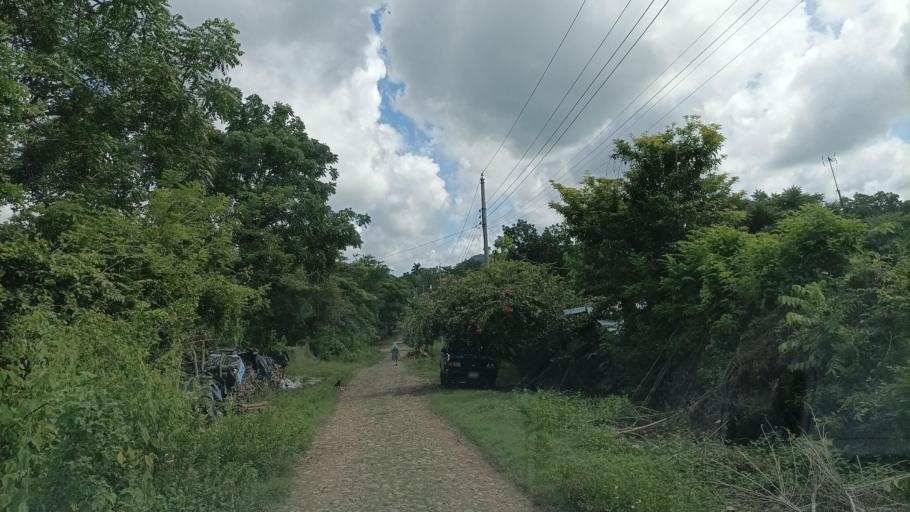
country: MX
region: Veracruz
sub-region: Tantoyuca
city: El Lindero
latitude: 21.1901
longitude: -98.1475
